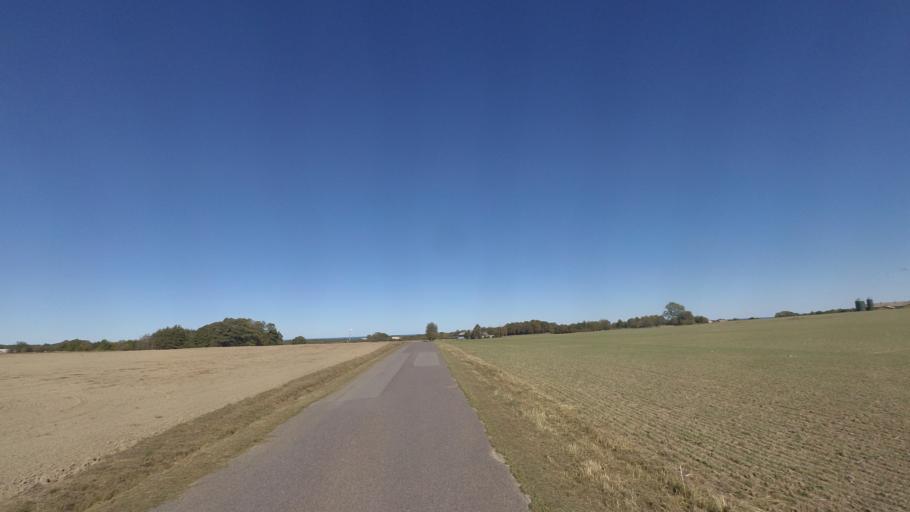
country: DK
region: Capital Region
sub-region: Bornholm Kommune
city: Nexo
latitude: 55.1181
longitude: 15.0458
